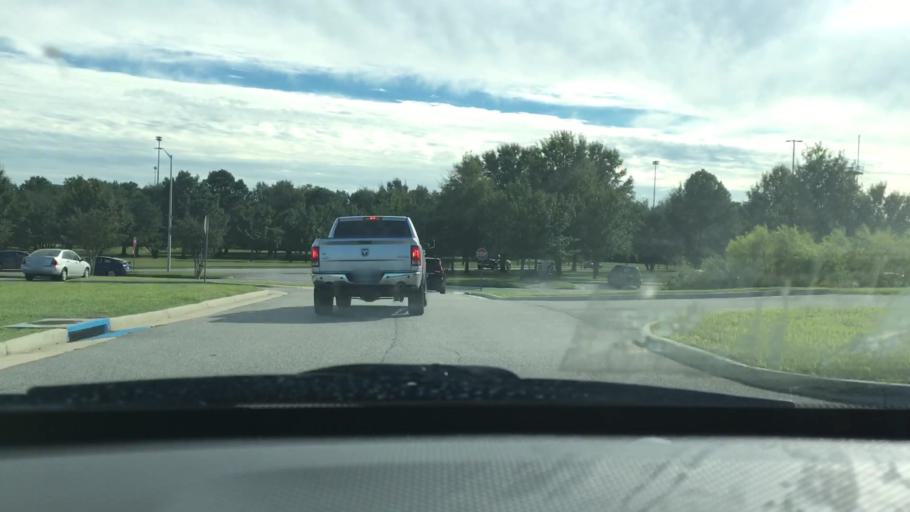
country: US
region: Virginia
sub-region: City of Portsmouth
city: Portsmouth Heights
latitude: 36.8828
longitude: -76.3585
